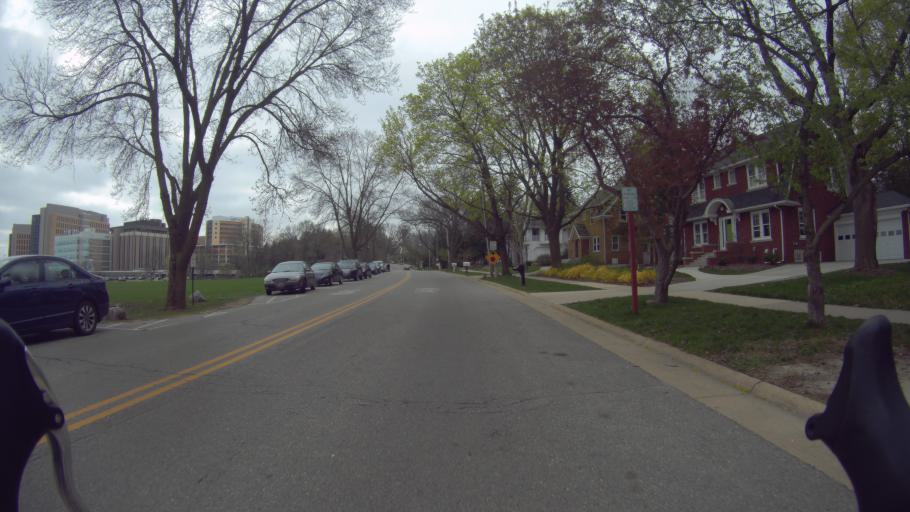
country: US
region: Wisconsin
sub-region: Dane County
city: Shorewood Hills
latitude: 43.0802
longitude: -89.4371
